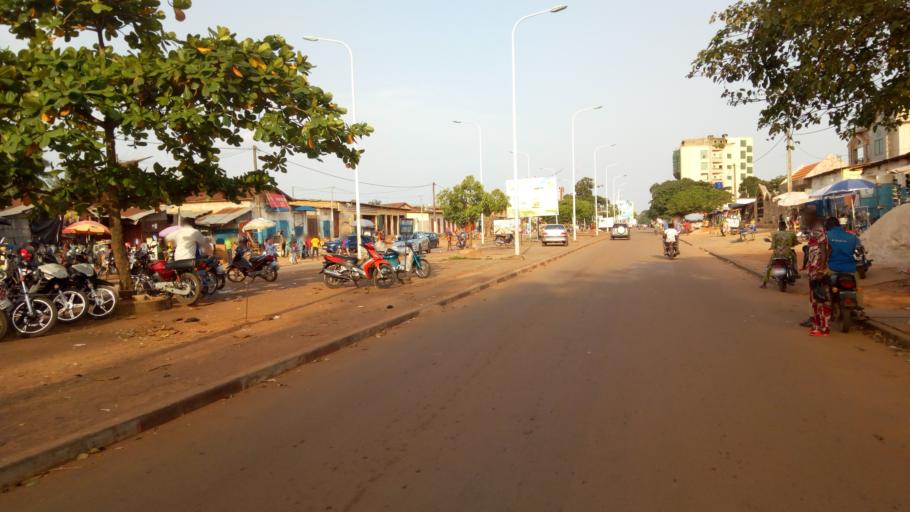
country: BJ
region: Queme
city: Porto-Novo
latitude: 6.4844
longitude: 2.6168
